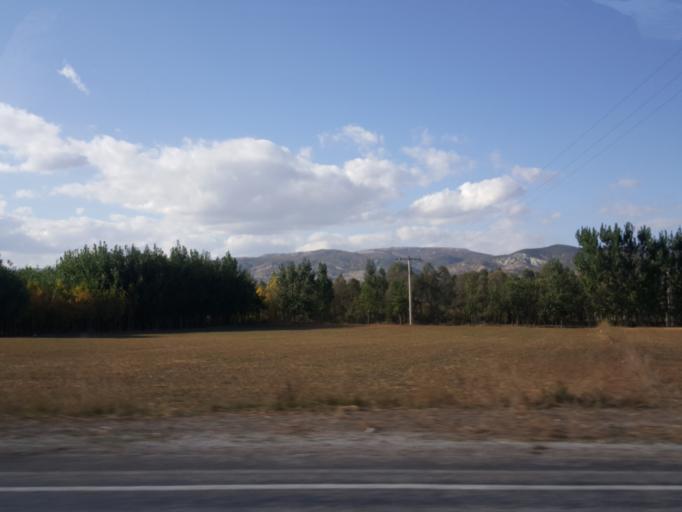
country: TR
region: Tokat
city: Yesilyurt
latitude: 40.0138
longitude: 36.2351
